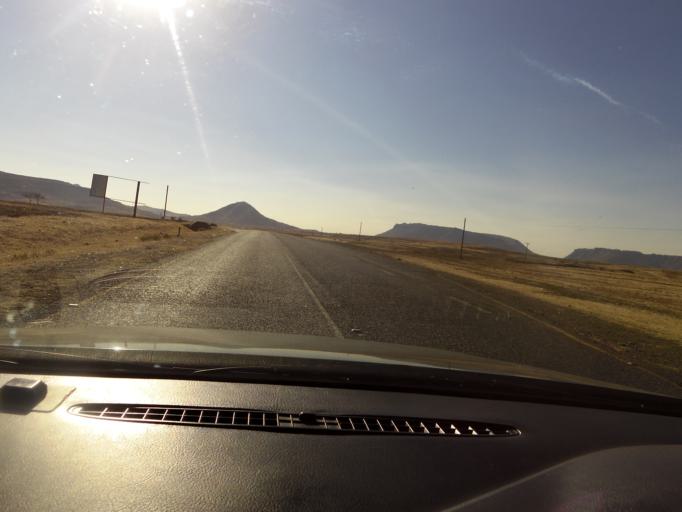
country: LS
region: Mafeteng
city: Mafeteng
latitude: -29.9757
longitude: 27.3188
